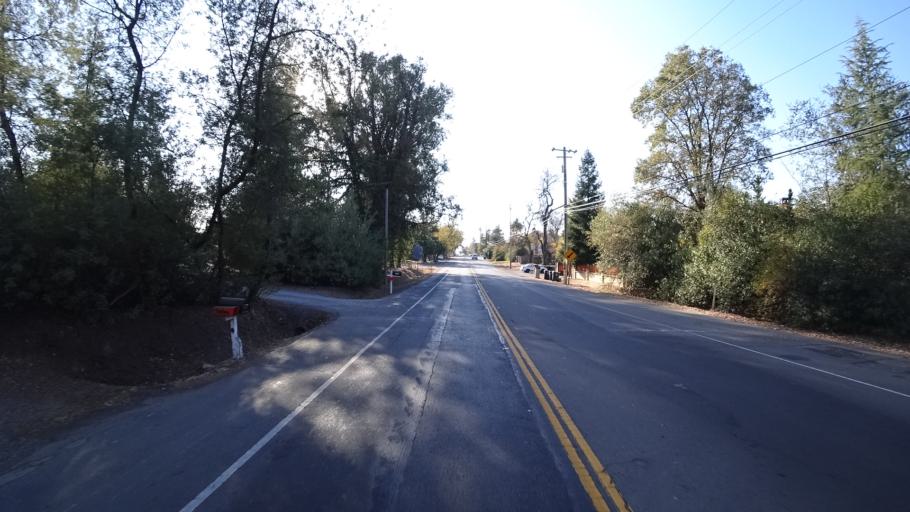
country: US
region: California
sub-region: Sacramento County
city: Citrus Heights
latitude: 38.7006
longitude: -121.2780
